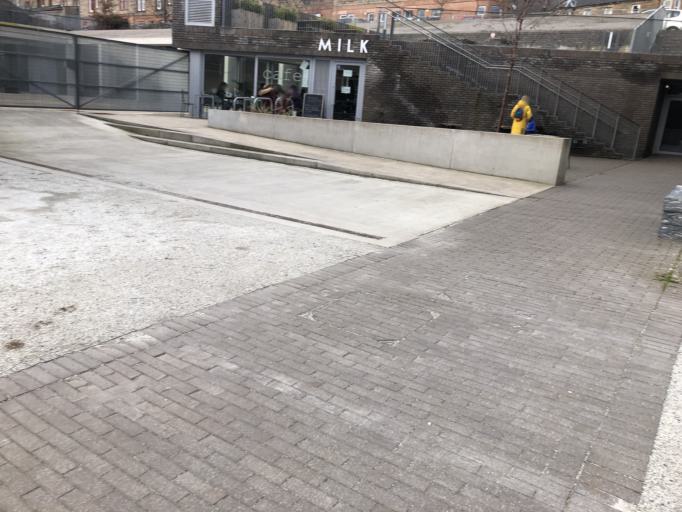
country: GB
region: Scotland
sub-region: Edinburgh
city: Edinburgh
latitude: 55.9785
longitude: -3.1907
